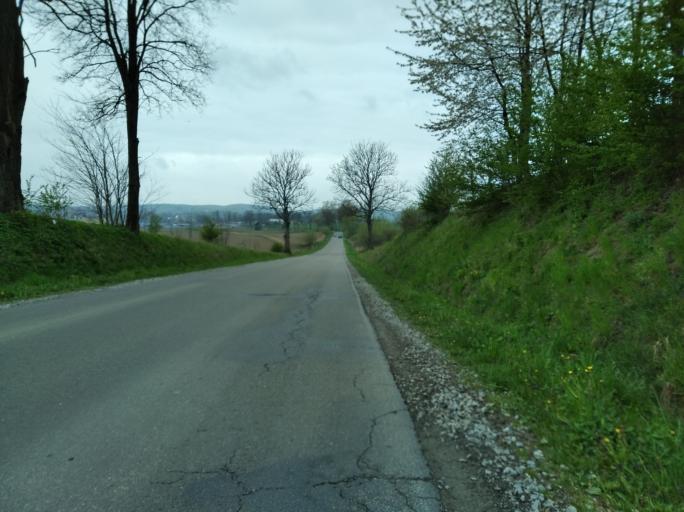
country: PL
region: Subcarpathian Voivodeship
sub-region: Powiat brzozowski
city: Brzozow
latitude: 49.7127
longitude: 22.0357
